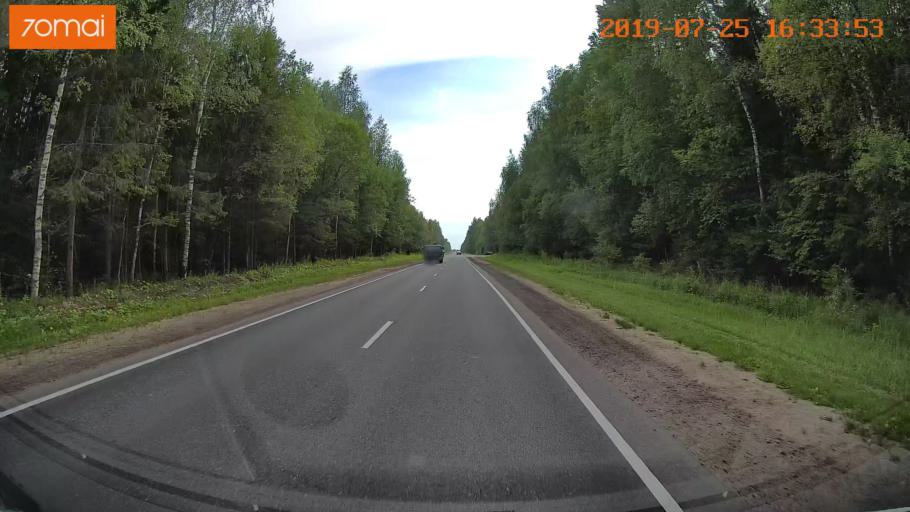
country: RU
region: Ivanovo
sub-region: Privolzhskiy Rayon
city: Ples
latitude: 57.4224
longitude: 41.4478
